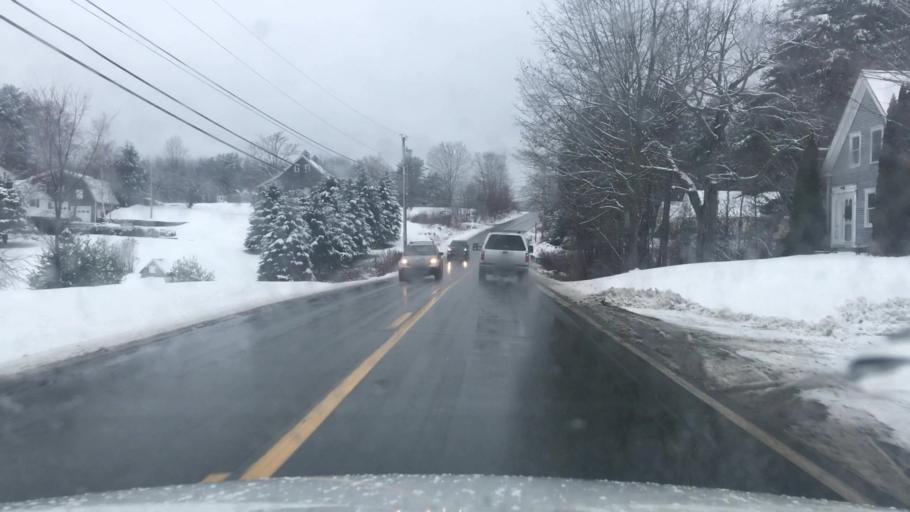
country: US
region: Maine
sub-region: Lincoln County
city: Jefferson
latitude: 44.2039
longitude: -69.4709
